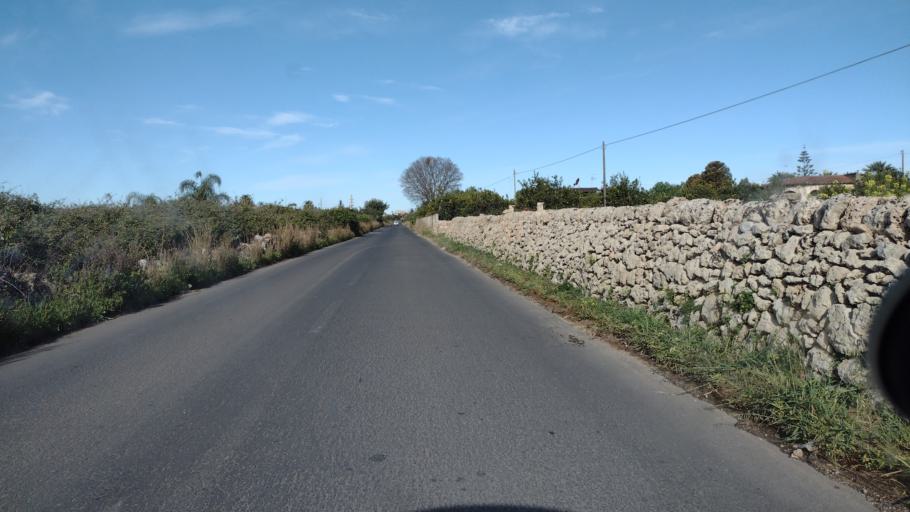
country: IT
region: Sicily
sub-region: Provincia di Siracusa
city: Avola
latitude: 36.8723
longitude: 15.1228
